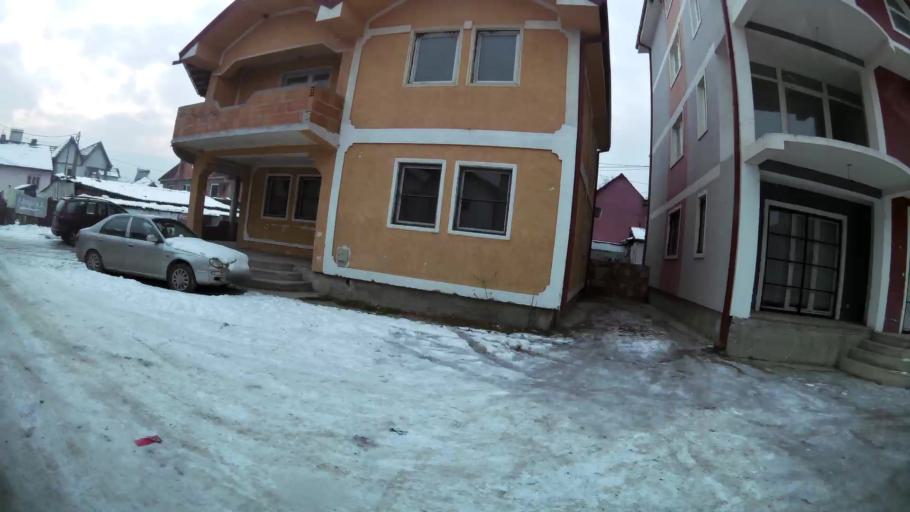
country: MK
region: Saraj
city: Saraj
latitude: 42.0168
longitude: 21.3591
